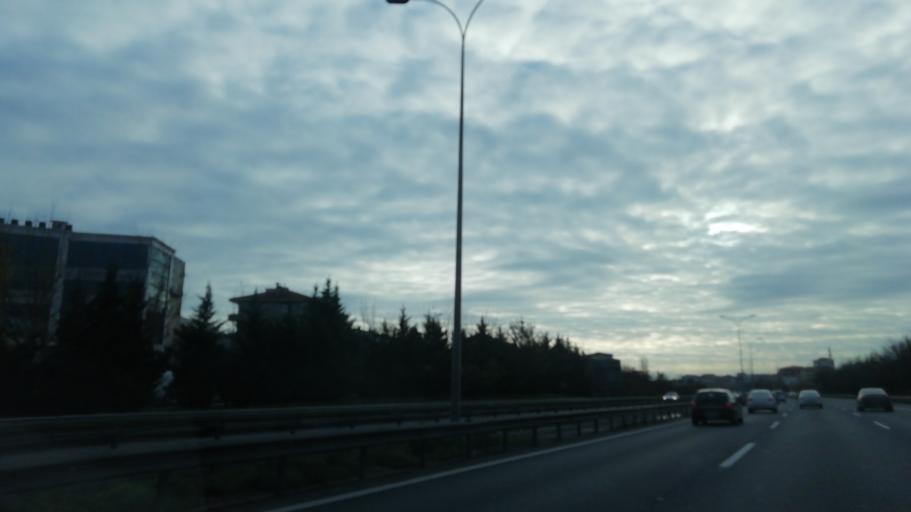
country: TR
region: Istanbul
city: Sultanbeyli
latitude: 40.9657
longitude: 29.2736
